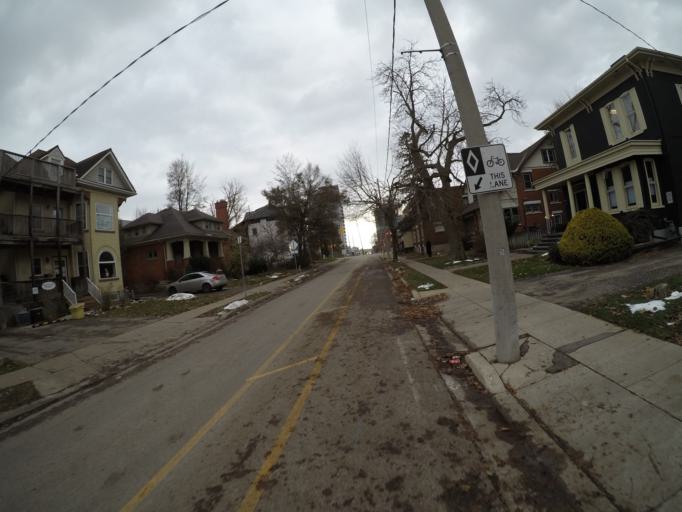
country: CA
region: Ontario
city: Waterloo
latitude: 43.4539
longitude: -80.4901
